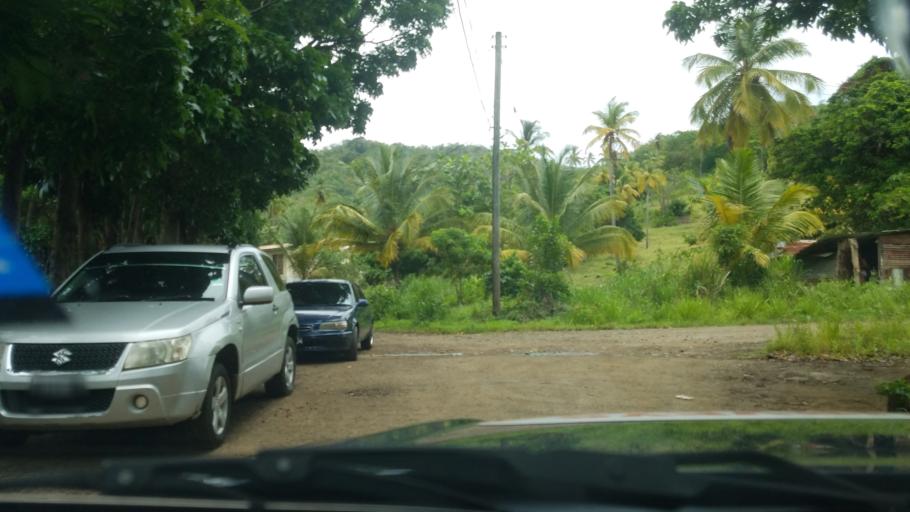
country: LC
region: Castries Quarter
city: Bisee
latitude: 14.0129
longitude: -60.9166
